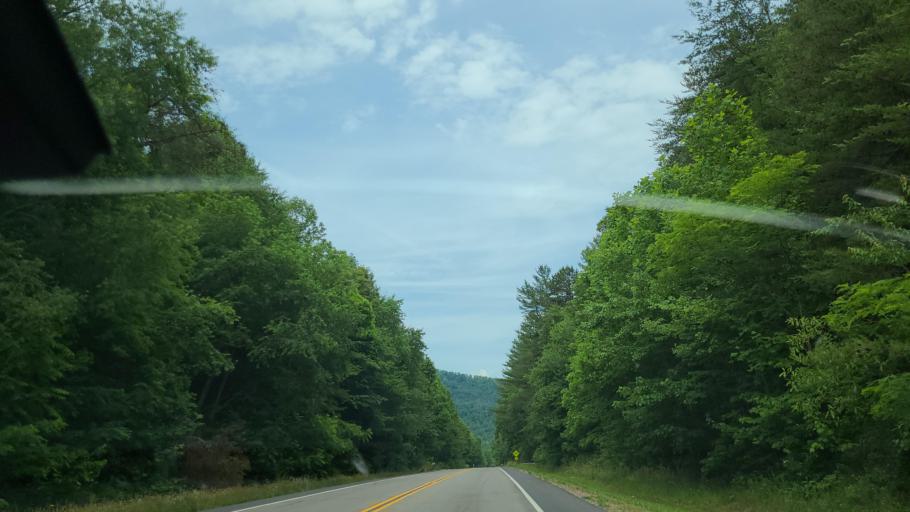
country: US
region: North Carolina
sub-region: Macon County
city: Franklin
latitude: 35.1455
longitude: -83.3062
